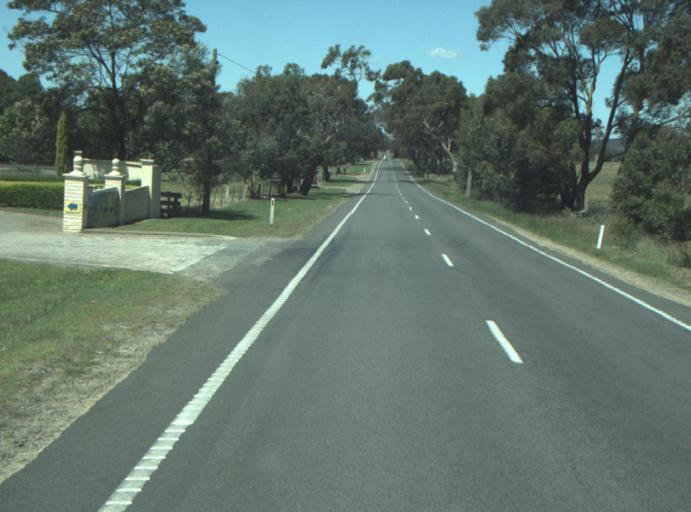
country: AU
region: Victoria
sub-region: Greater Geelong
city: Lara
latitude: -37.8899
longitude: 144.2563
